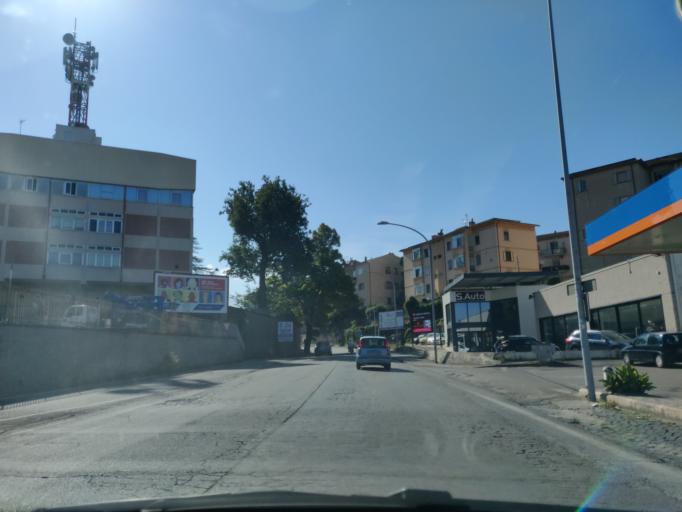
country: IT
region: Latium
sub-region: Provincia di Viterbo
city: Viterbo
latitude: 42.4260
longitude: 12.0992
